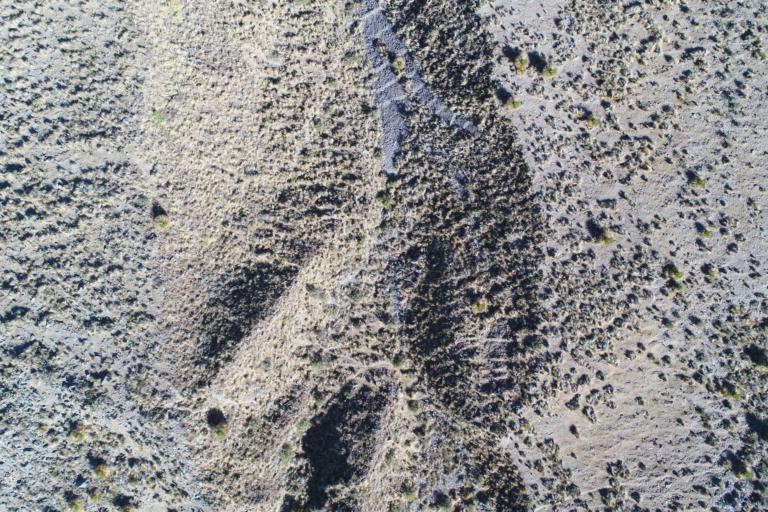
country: BO
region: La Paz
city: Viloco
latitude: -16.8087
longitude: -67.5507
